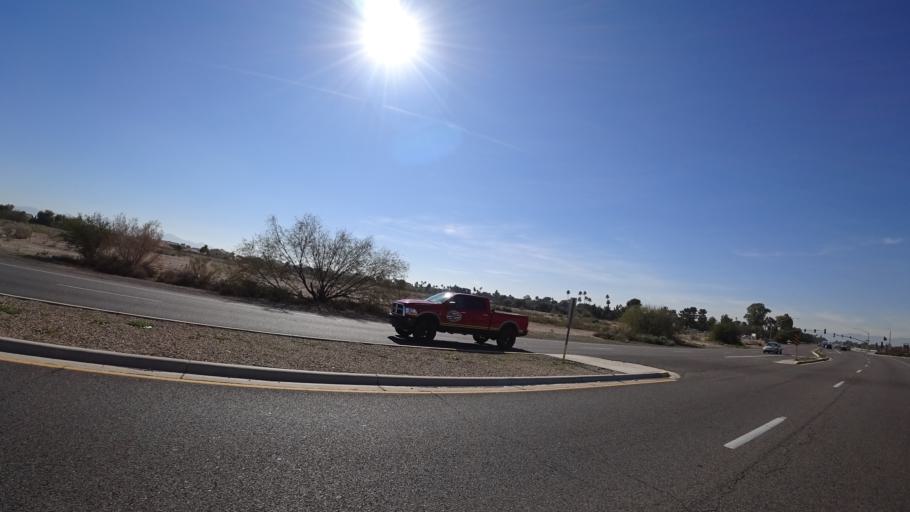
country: US
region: Arizona
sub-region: Maricopa County
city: Litchfield Park
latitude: 33.5078
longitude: -112.3386
